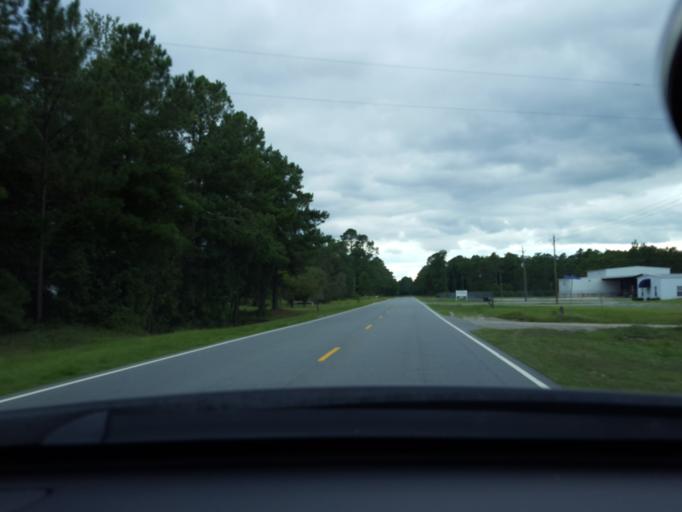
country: US
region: North Carolina
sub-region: Bladen County
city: Elizabethtown
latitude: 34.7079
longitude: -78.4639
